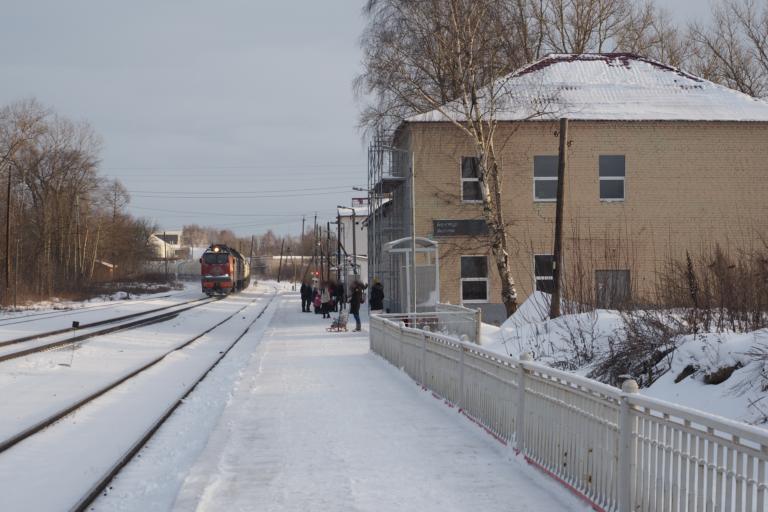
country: RU
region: Tverskaya
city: Bezhetsk
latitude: 57.7978
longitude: 36.6928
